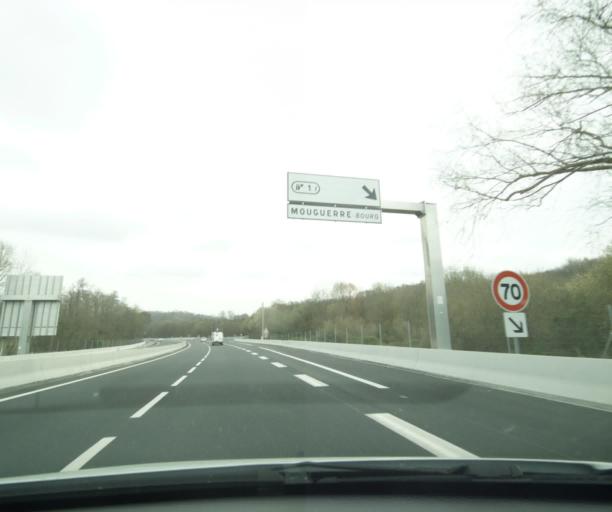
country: FR
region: Aquitaine
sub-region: Departement des Pyrenees-Atlantiques
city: Mouguerre
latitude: 43.4654
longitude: -1.4301
